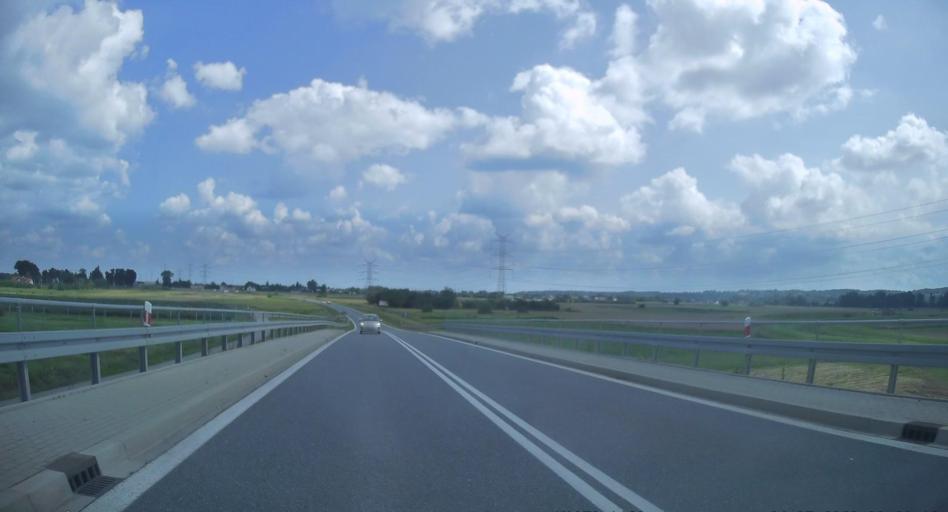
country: PL
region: Lesser Poland Voivodeship
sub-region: Powiat tarnowski
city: Wojnicz
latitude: 49.9525
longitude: 20.8508
